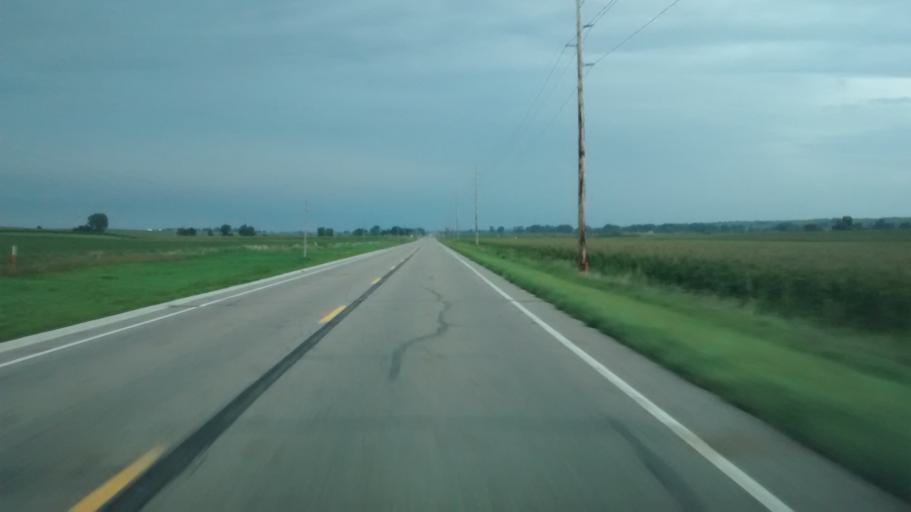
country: US
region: Iowa
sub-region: Plymouth County
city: Kingsley
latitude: 42.5518
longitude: -96.0189
